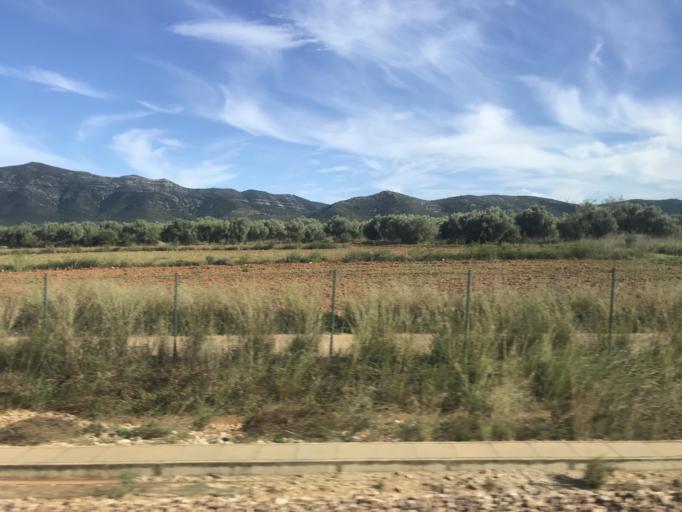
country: ES
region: Catalonia
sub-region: Provincia de Tarragona
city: Ulldecona
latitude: 40.6160
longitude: 0.4710
